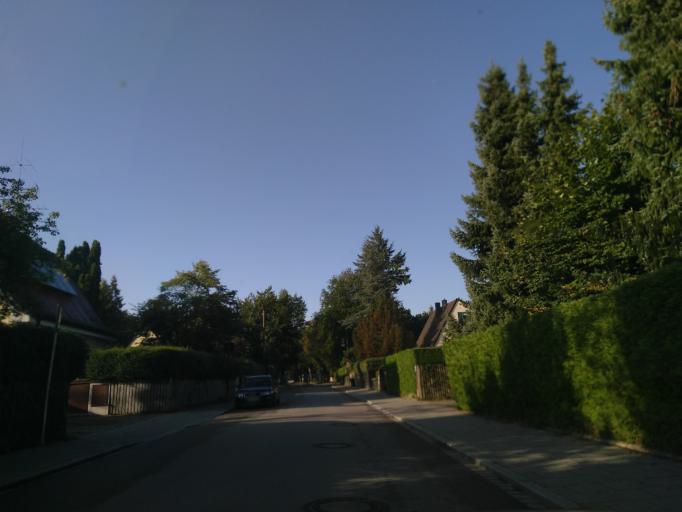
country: DE
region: Bavaria
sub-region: Upper Bavaria
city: Pullach im Isartal
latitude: 48.0496
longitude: 11.5112
